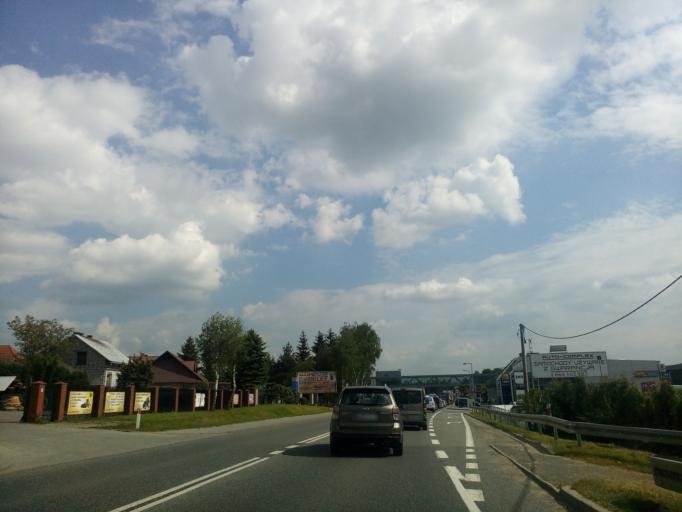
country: PL
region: Lesser Poland Voivodeship
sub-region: Powiat nowosadecki
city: Chelmiec
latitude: 49.6712
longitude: 20.6858
